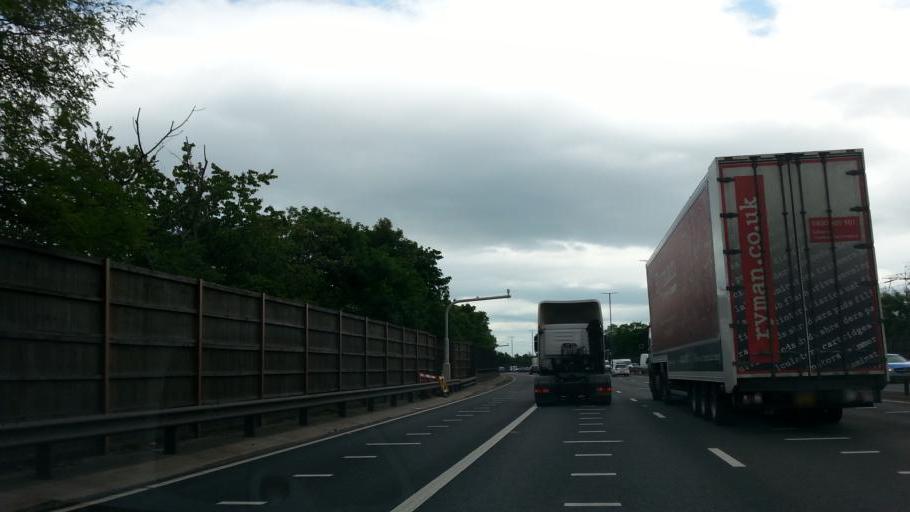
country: GB
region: England
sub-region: City and Borough of Birmingham
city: Hockley
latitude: 52.5296
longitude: -1.8965
